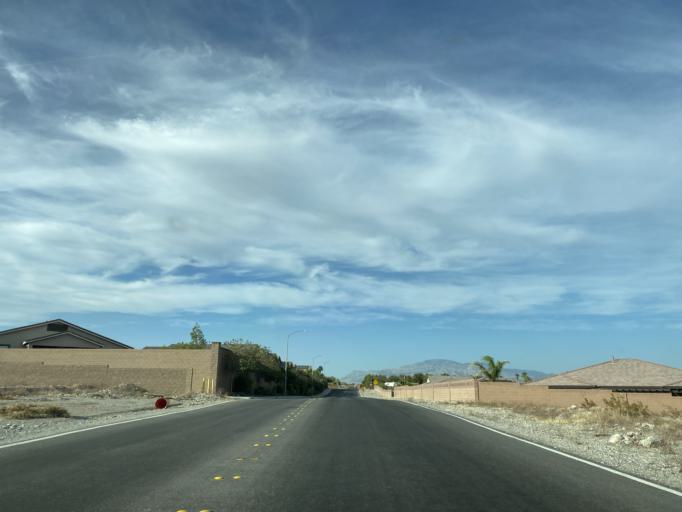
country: US
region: Nevada
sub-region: Clark County
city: Summerlin South
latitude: 36.2861
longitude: -115.3126
